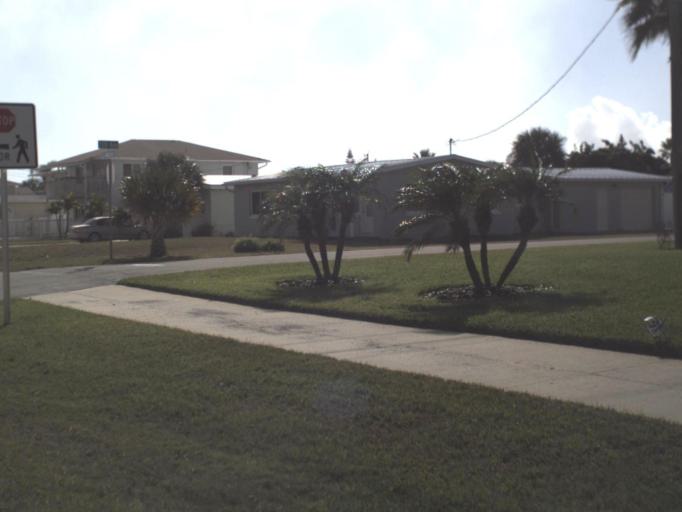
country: US
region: Florida
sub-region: Volusia County
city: Edgewater
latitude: 29.0193
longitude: -80.8858
